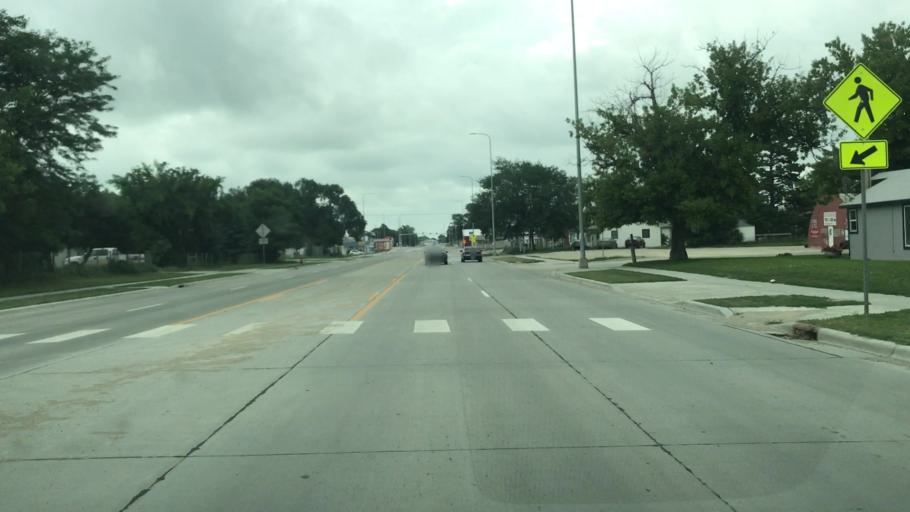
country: US
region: South Dakota
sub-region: Todd County
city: Mission
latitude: 43.3057
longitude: -100.6642
